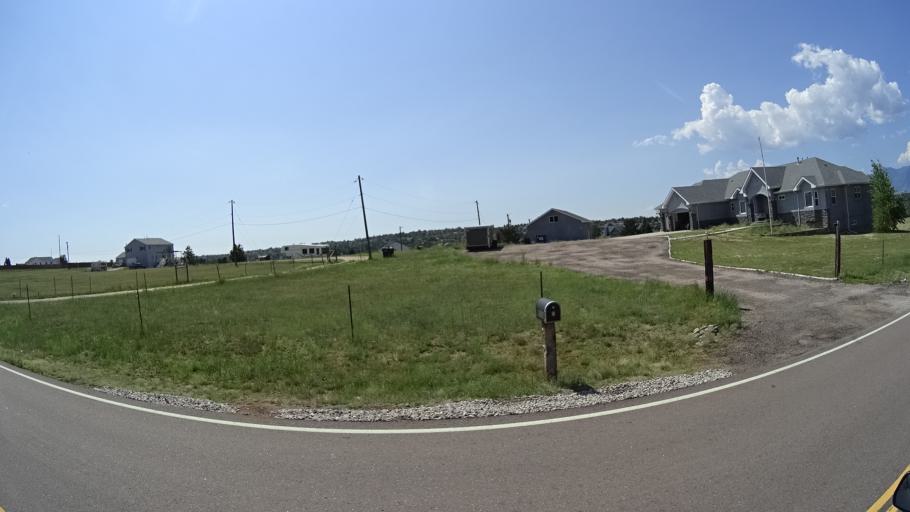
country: US
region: Colorado
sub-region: El Paso County
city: Air Force Academy
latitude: 38.9357
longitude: -104.7773
